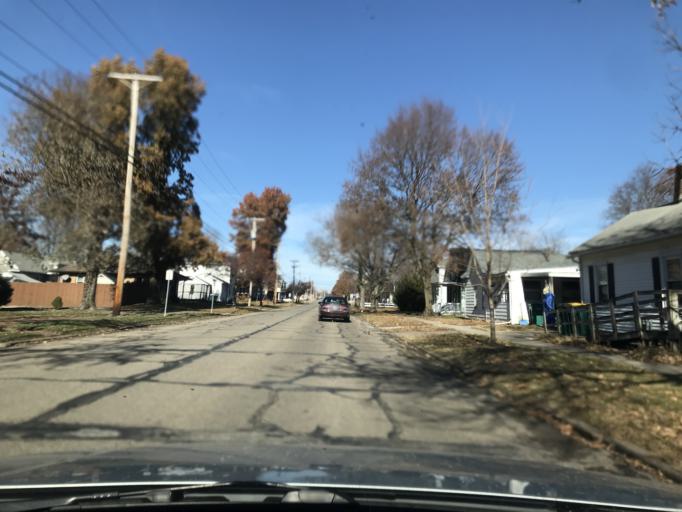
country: US
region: Illinois
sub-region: McDonough County
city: Macomb
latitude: 40.4554
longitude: -90.6672
